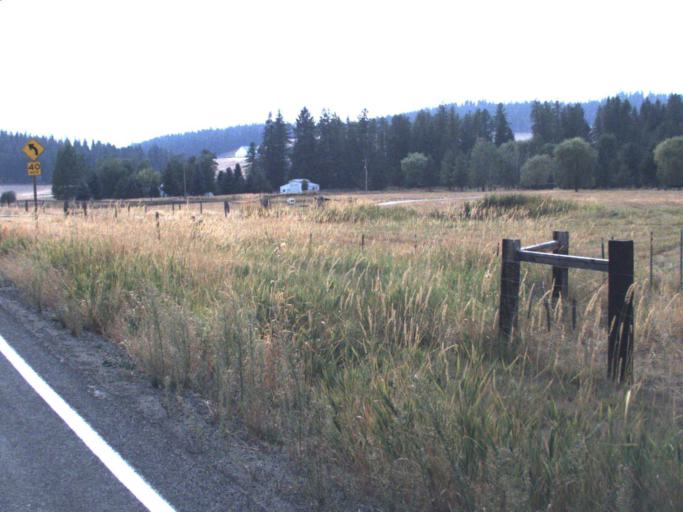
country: US
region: Washington
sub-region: Spokane County
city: Trentwood
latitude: 47.8178
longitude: -117.2138
